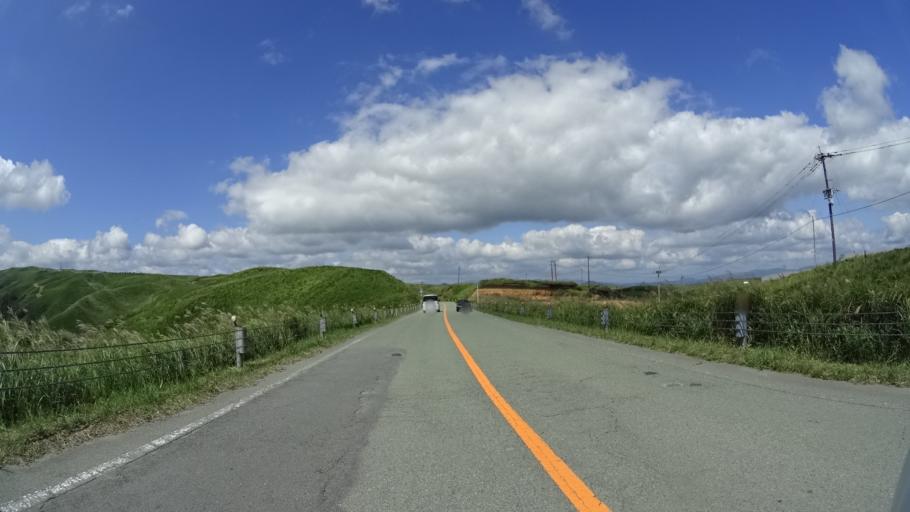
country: JP
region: Kumamoto
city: Aso
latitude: 32.9991
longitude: 131.0815
